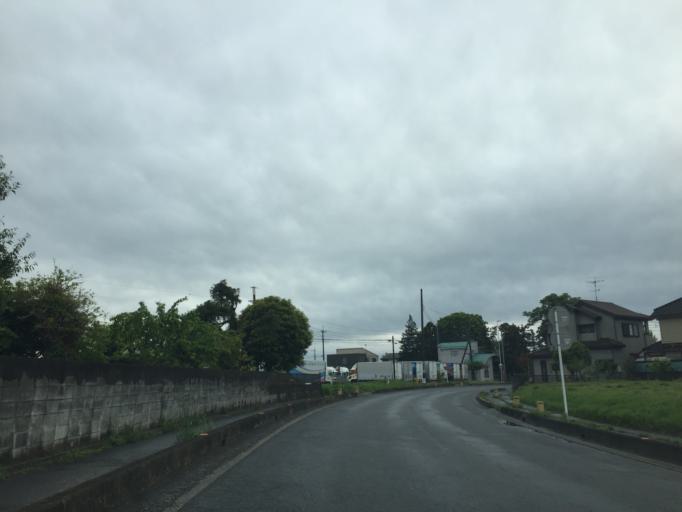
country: JP
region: Saitama
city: Shiki
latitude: 35.8638
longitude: 139.5698
